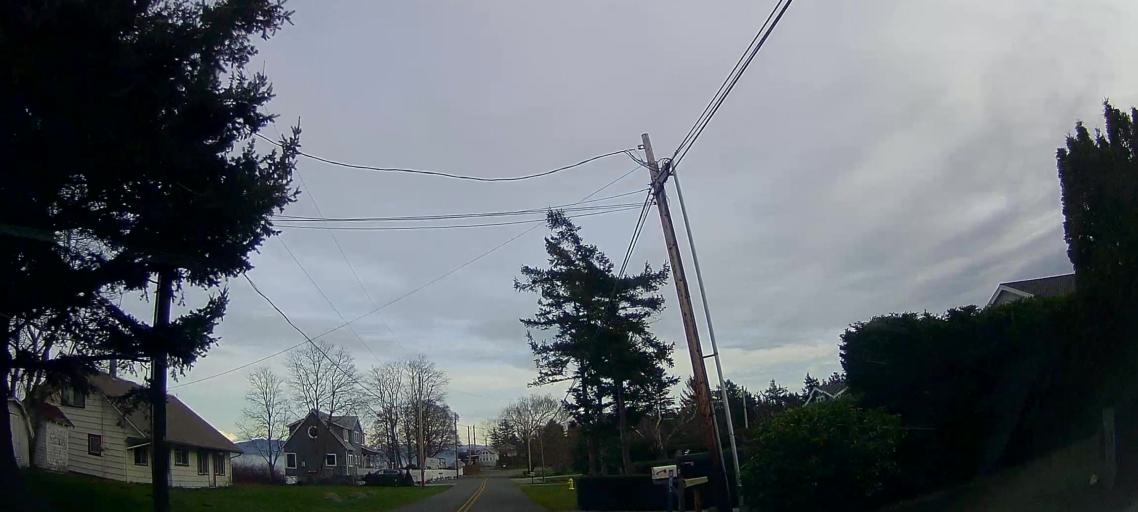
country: US
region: Washington
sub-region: Skagit County
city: Anacortes
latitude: 48.5756
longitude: -122.5380
